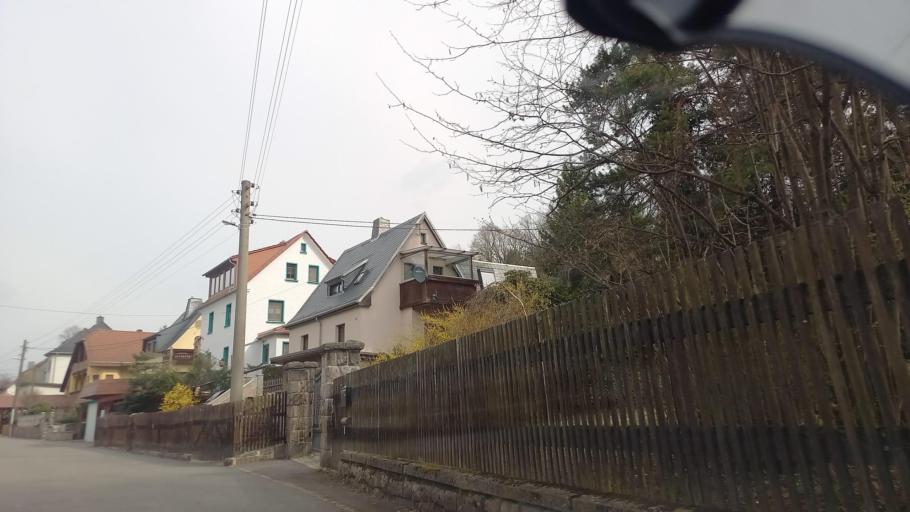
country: DE
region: Saxony
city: Kirchberg
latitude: 50.6302
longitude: 12.5237
